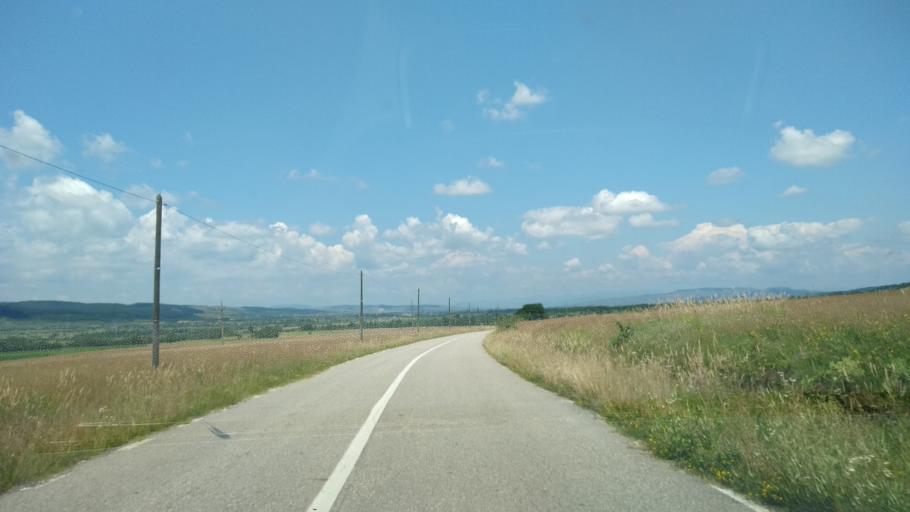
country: RO
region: Hunedoara
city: Berca
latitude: 45.6116
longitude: 23.0229
